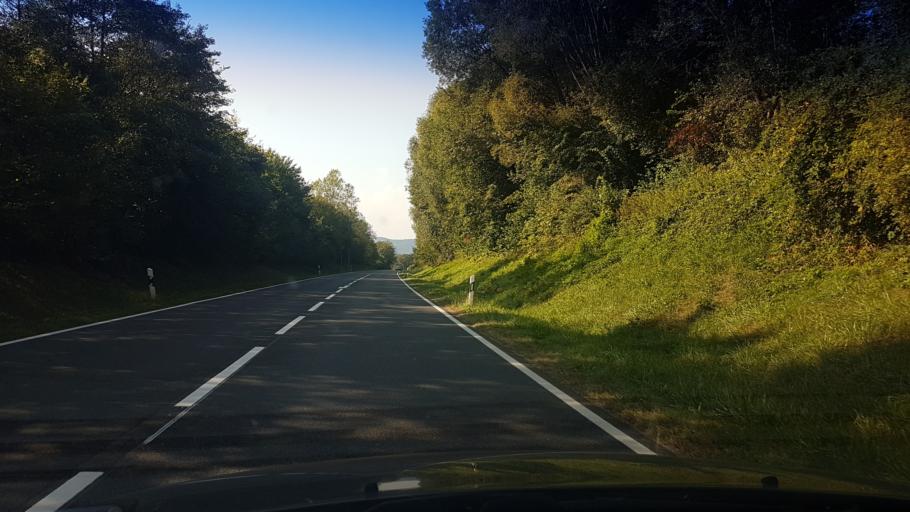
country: DE
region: Bavaria
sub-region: Upper Franconia
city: Bad Staffelstein
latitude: 50.0825
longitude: 11.0225
